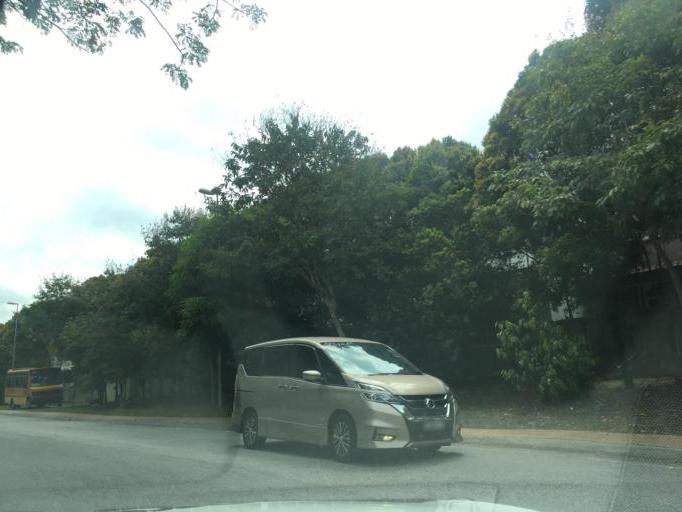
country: MY
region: Selangor
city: Shah Alam
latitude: 3.0810
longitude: 101.4836
